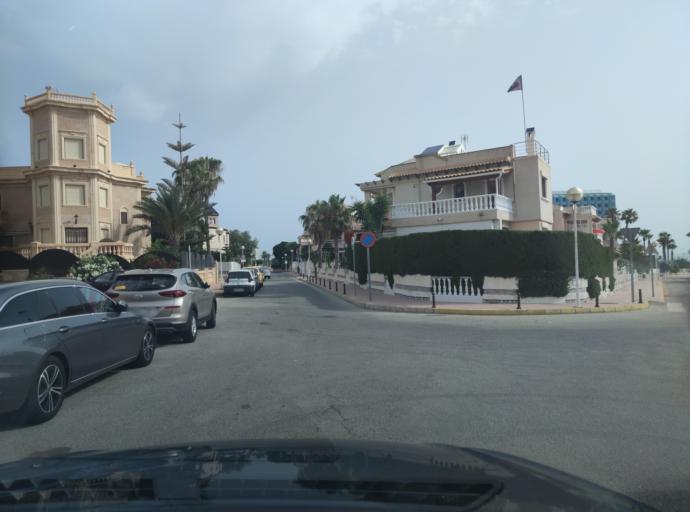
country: ES
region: Valencia
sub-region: Provincia de Alicante
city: Guardamar del Segura
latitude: 38.0637
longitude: -0.6526
